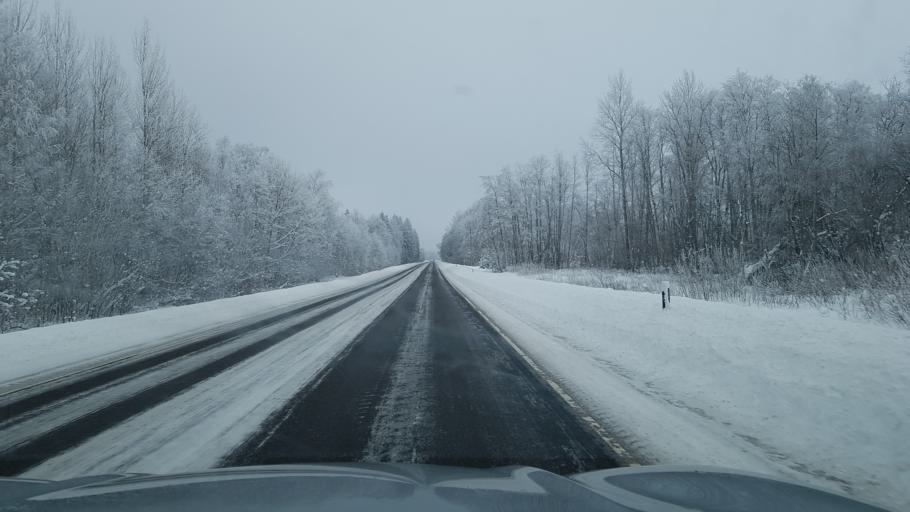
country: EE
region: Ida-Virumaa
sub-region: Johvi vald
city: Johvi
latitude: 59.2754
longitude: 27.3889
